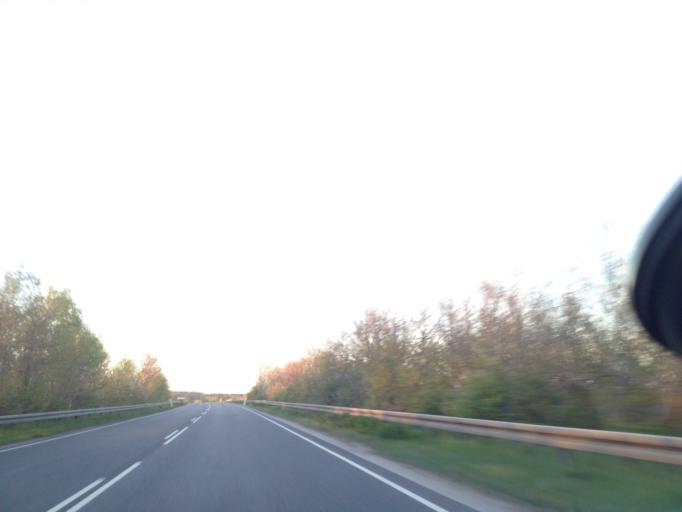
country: DK
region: Capital Region
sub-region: Frederikssund Kommune
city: Jaegerspris
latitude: 55.8208
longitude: 12.0045
